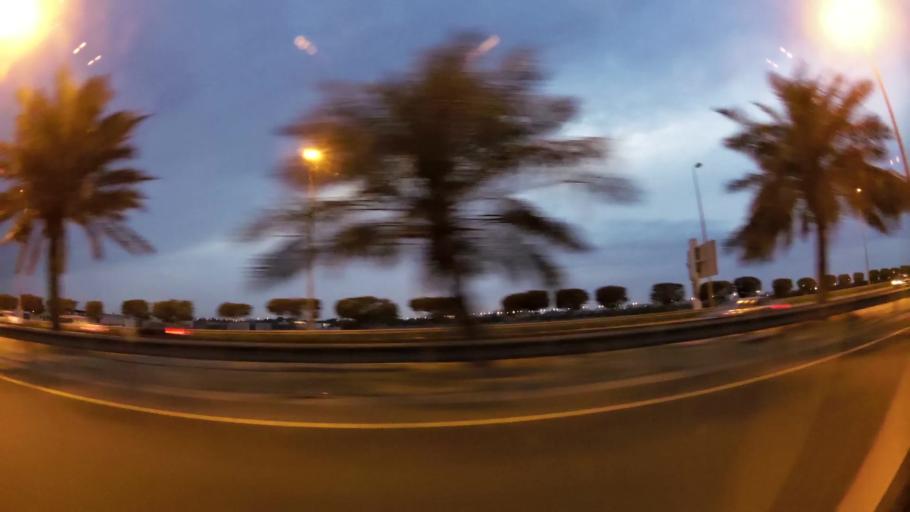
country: BH
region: Northern
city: Madinat `Isa
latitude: 26.1741
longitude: 50.5024
